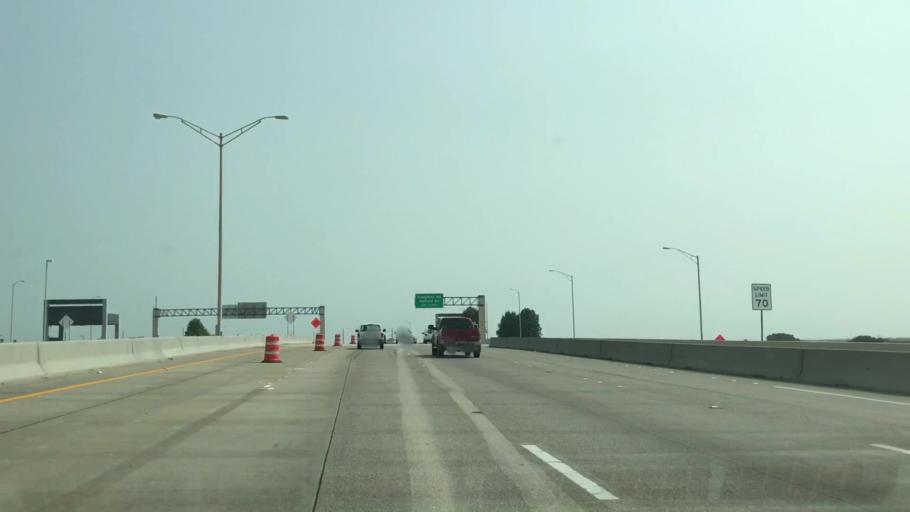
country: US
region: Texas
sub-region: Collin County
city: Plano
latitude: 32.9870
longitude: -96.6667
